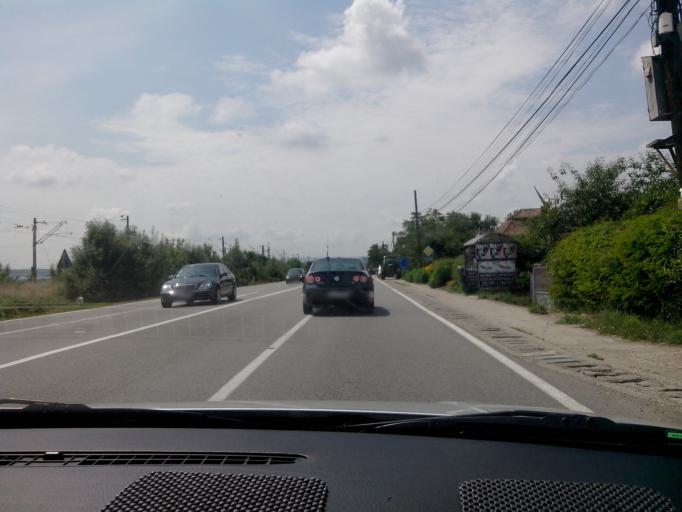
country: RO
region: Cluj
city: Jucu Herghelia
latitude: 46.8592
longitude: 23.7611
